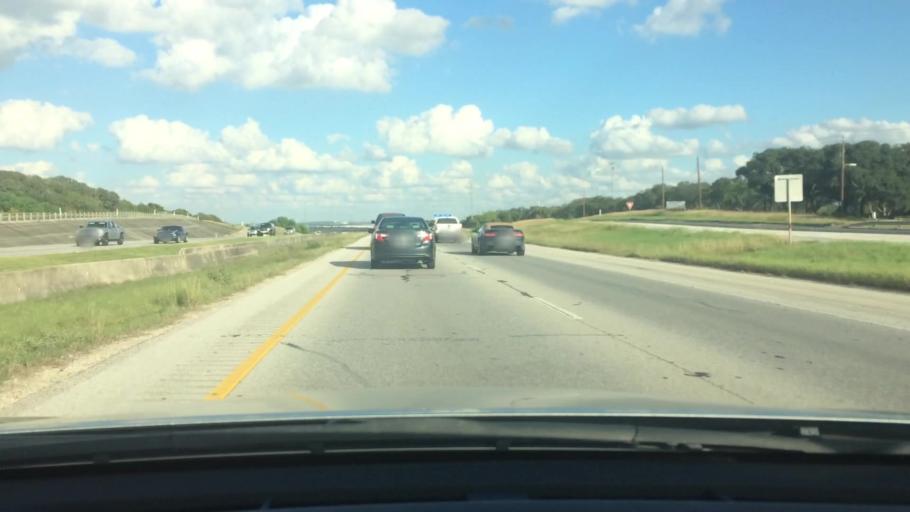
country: US
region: Texas
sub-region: Bexar County
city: Live Oak
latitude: 29.6026
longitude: -98.3734
